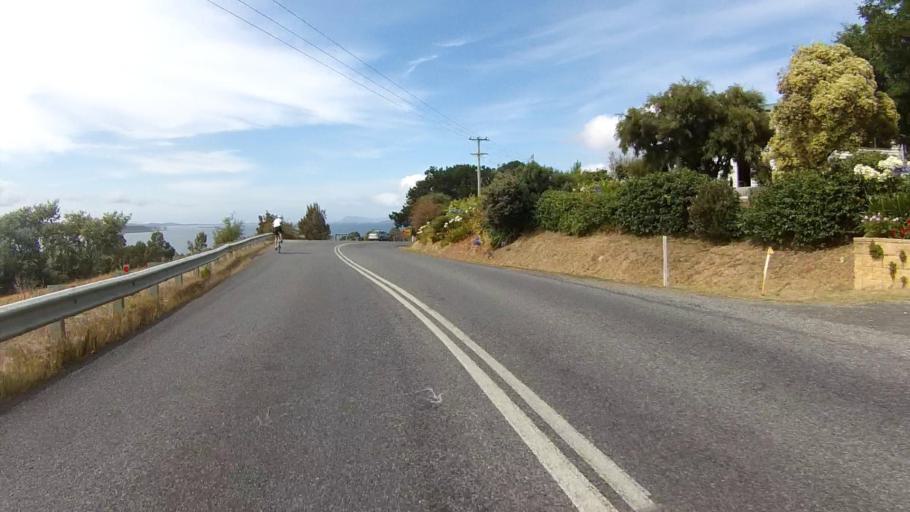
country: AU
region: Tasmania
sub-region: Kingborough
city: Kettering
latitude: -43.1418
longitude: 147.2433
